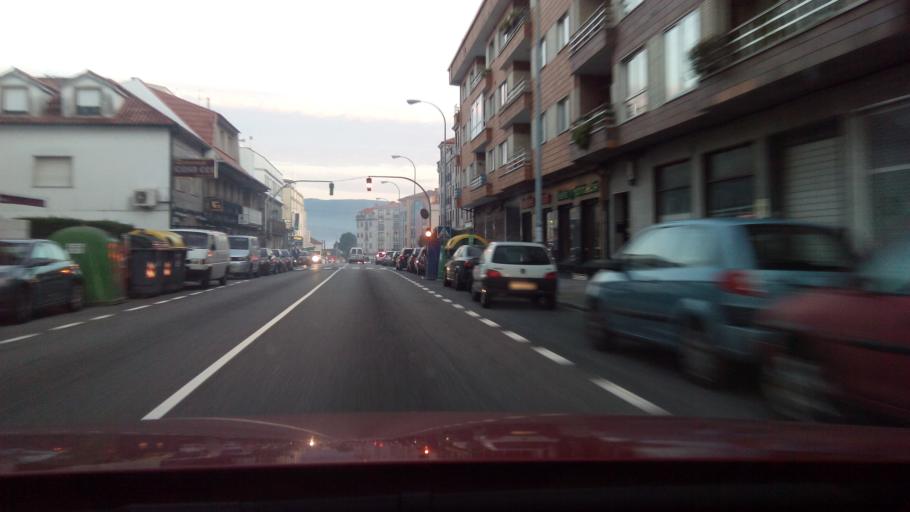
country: ES
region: Galicia
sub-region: Provincia de Pontevedra
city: Poio
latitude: 42.4326
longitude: -8.6672
